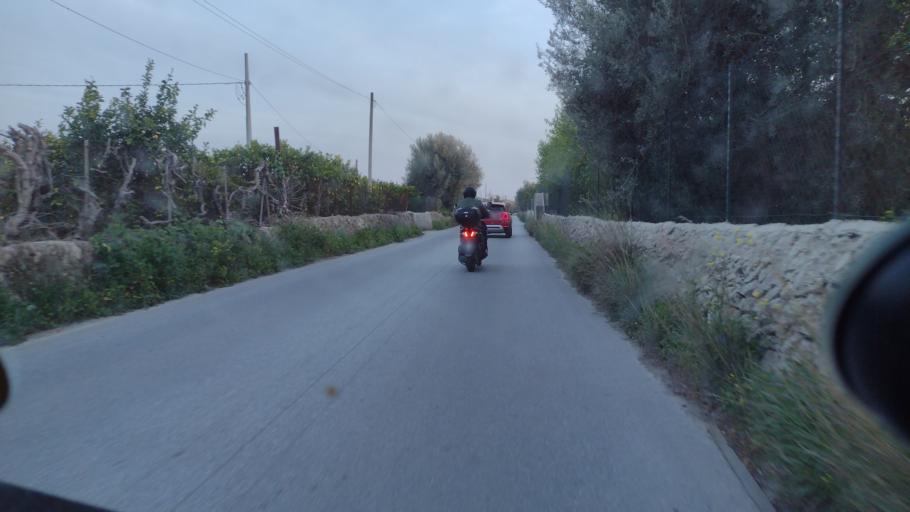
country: IT
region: Sicily
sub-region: Provincia di Siracusa
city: Avola
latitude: 36.8856
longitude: 15.1310
